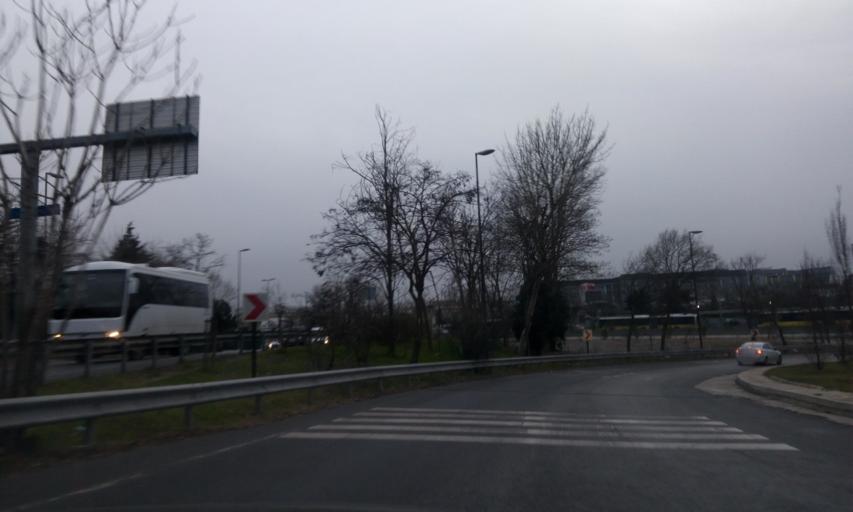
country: TR
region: Istanbul
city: UEskuedar
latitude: 41.0221
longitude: 29.0500
